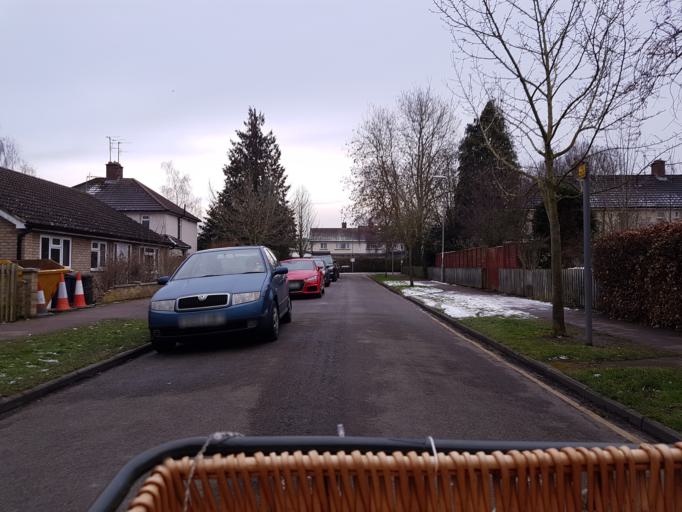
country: GB
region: England
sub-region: Cambridgeshire
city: Cambridge
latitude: 52.1832
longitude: 0.1454
